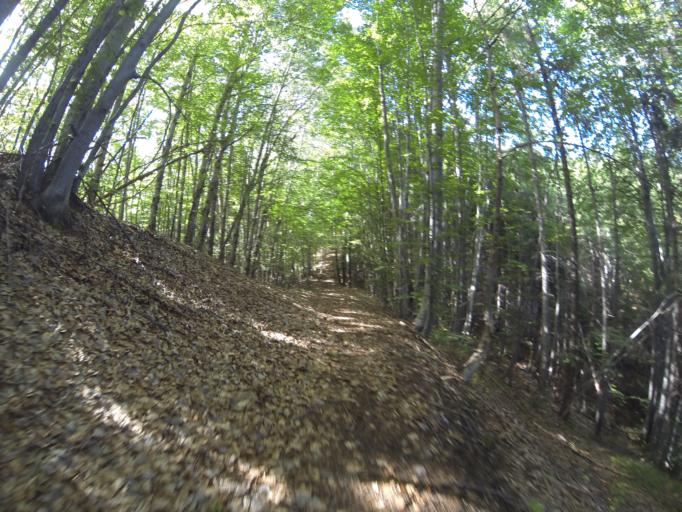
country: RO
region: Valcea
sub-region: Comuna Barbatesti
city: Barbatesti
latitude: 45.2515
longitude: 24.1580
